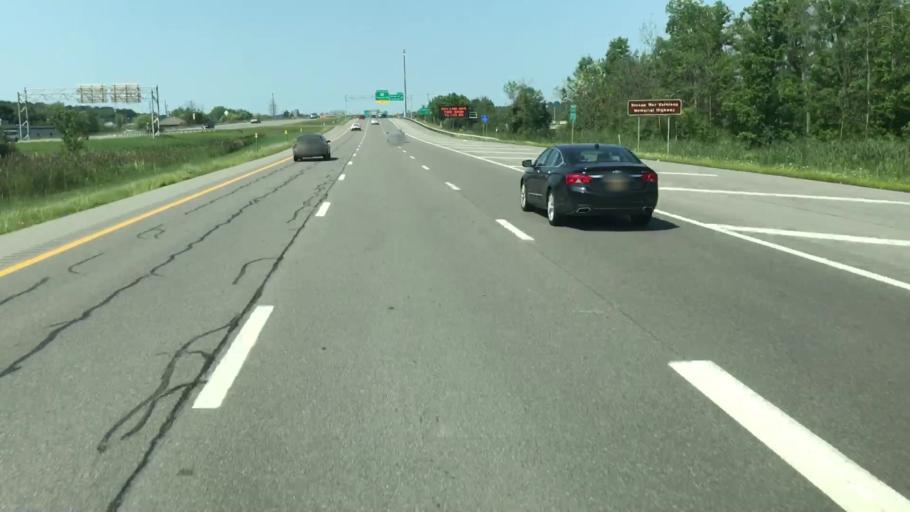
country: US
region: New York
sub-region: Onondaga County
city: East Syracuse
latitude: 43.0570
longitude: -76.0617
